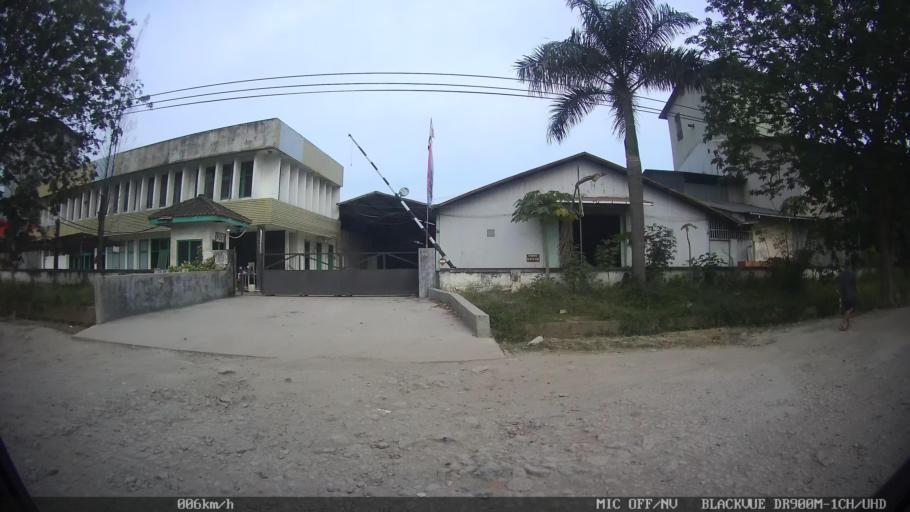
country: ID
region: Lampung
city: Panjang
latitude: -5.4499
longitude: 105.3095
